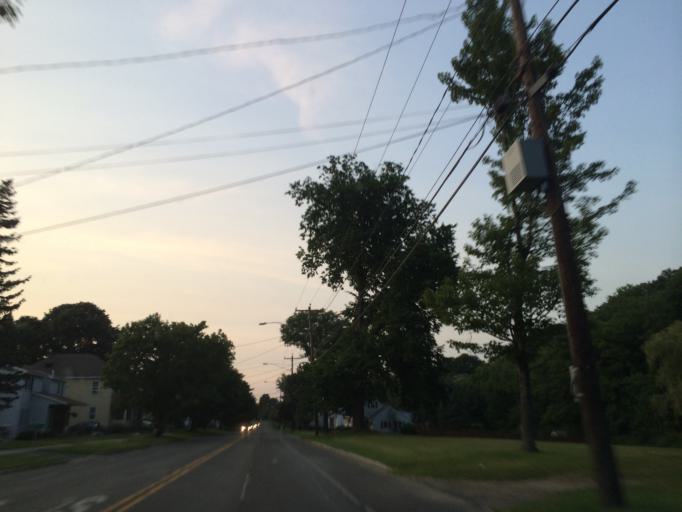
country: US
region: Massachusetts
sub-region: Berkshire County
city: Pittsfield
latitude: 42.4683
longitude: -73.2454
